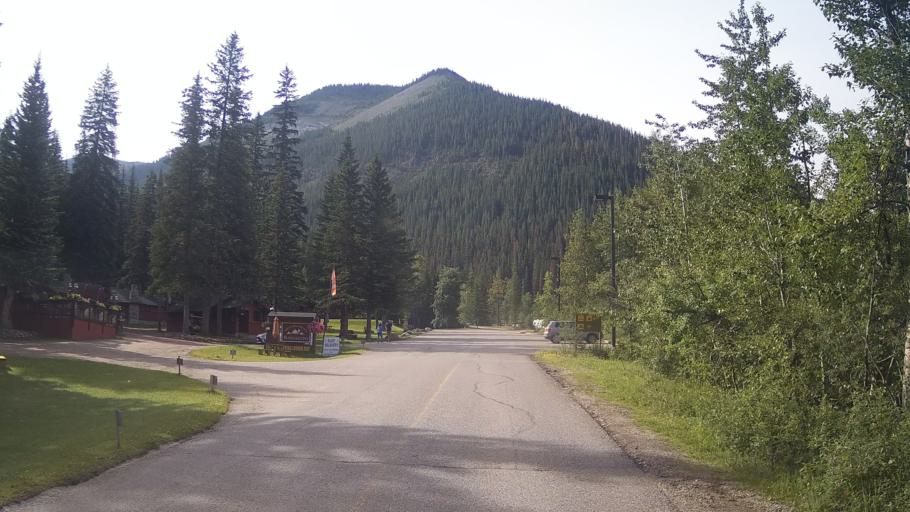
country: CA
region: Alberta
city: Hinton
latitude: 53.1326
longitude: -117.7717
